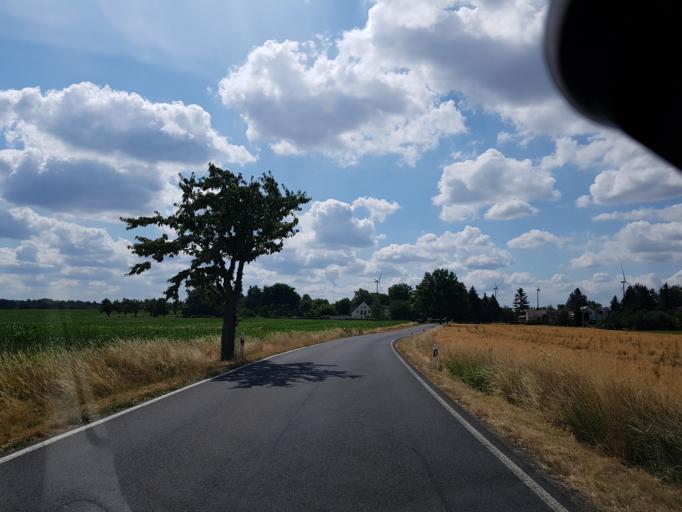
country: DE
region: Brandenburg
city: Drebkau
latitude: 51.6695
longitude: 14.2829
